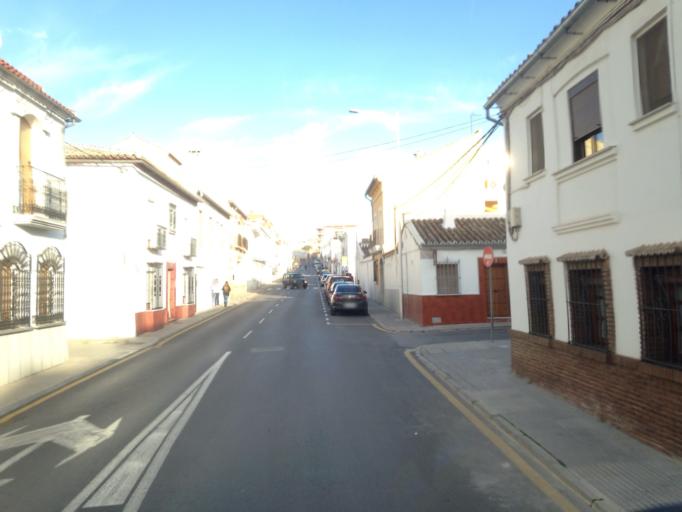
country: ES
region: Andalusia
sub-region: Provincia de Malaga
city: Antequera
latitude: 37.0212
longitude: -4.5698
